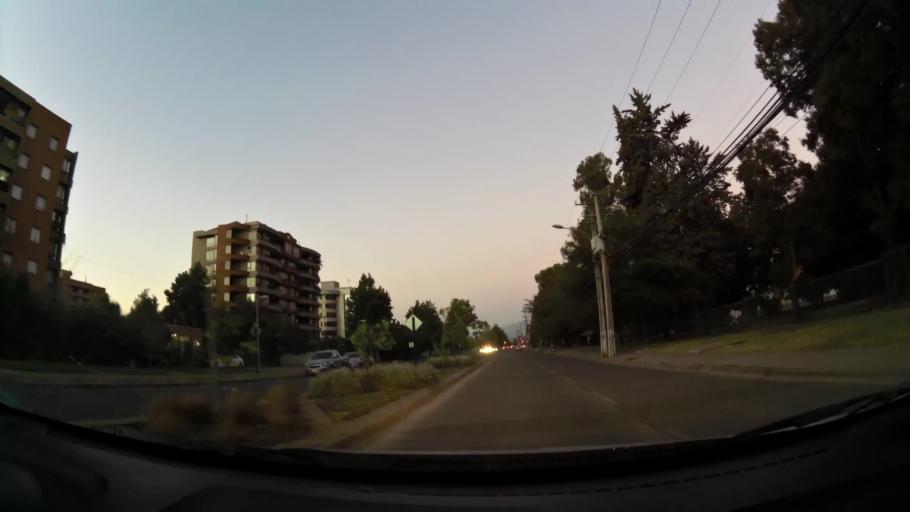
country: CL
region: O'Higgins
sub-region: Provincia de Cachapoal
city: Rancagua
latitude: -34.1881
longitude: -70.7233
